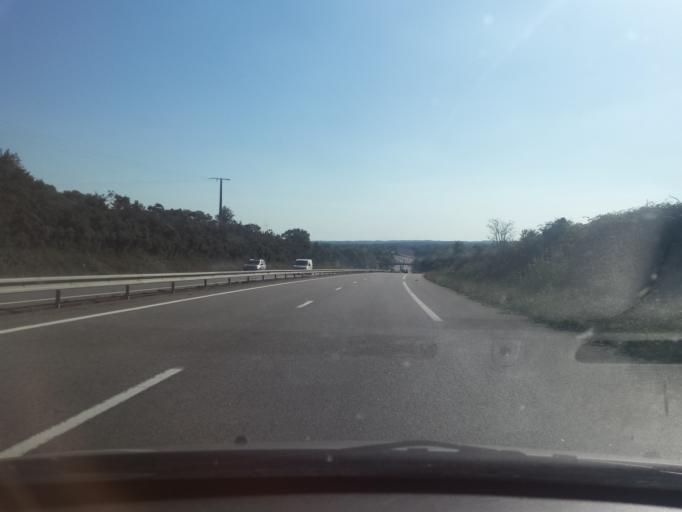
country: FR
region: Brittany
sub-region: Departement du Morbihan
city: Meucon
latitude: 47.7184
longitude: -2.7589
